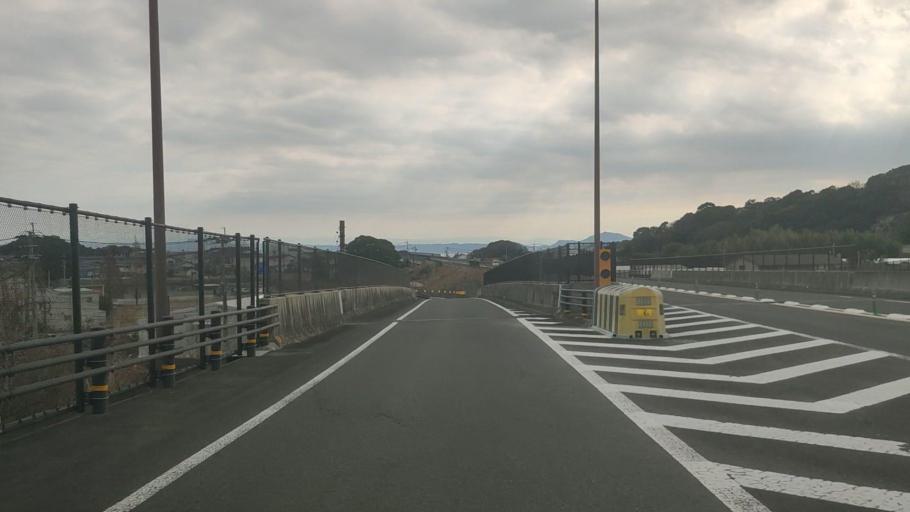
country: JP
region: Nagasaki
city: Shimabara
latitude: 32.7630
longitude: 130.3624
